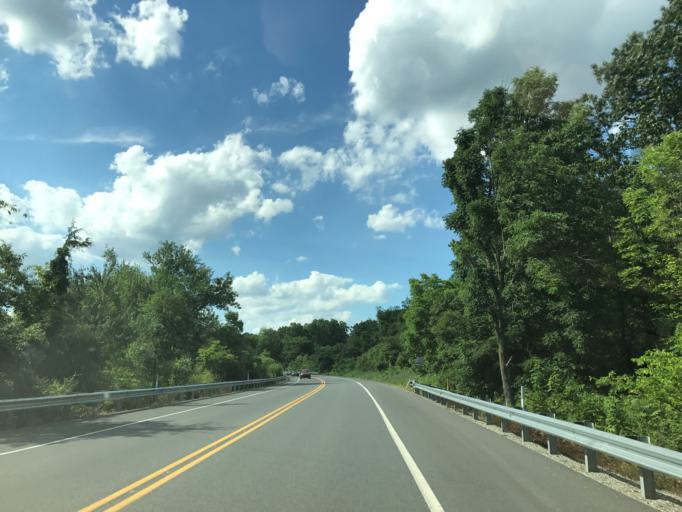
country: US
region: Pennsylvania
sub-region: York County
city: Parkville
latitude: 39.7748
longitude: -76.8794
